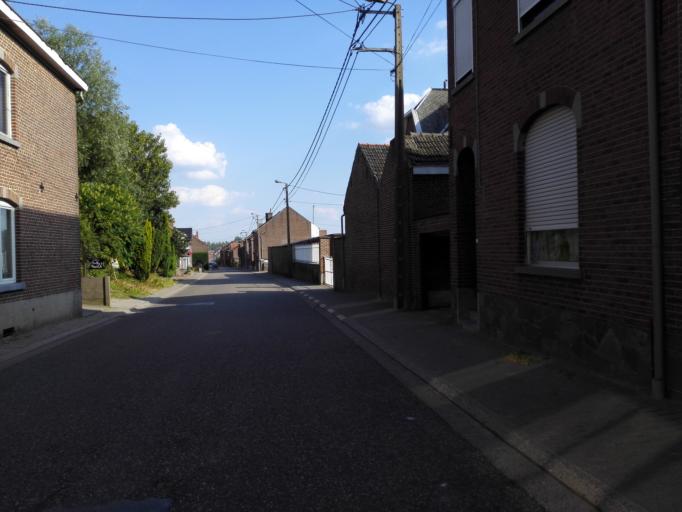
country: BE
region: Flanders
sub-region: Provincie Vlaams-Brabant
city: Tienen
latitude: 50.8274
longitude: 4.9924
